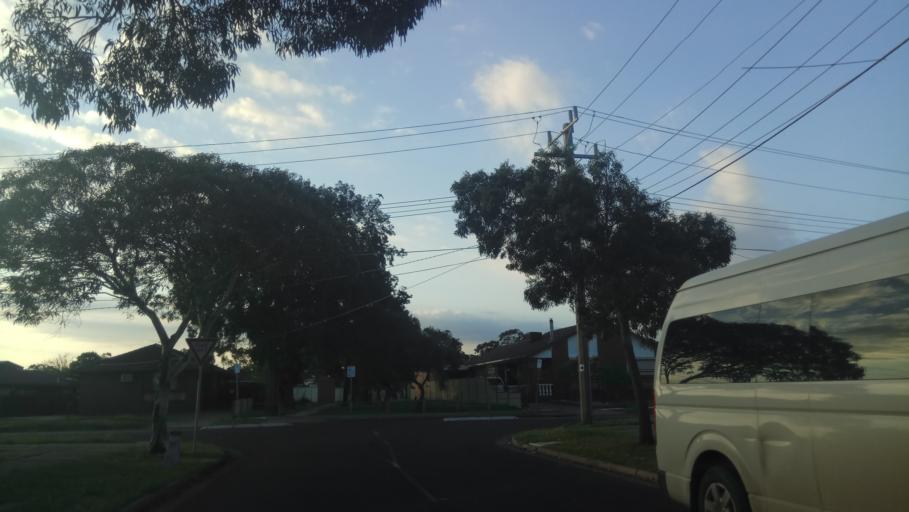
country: AU
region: Victoria
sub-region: Hobsons Bay
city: Altona Meadows
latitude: -37.8787
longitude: 144.7905
